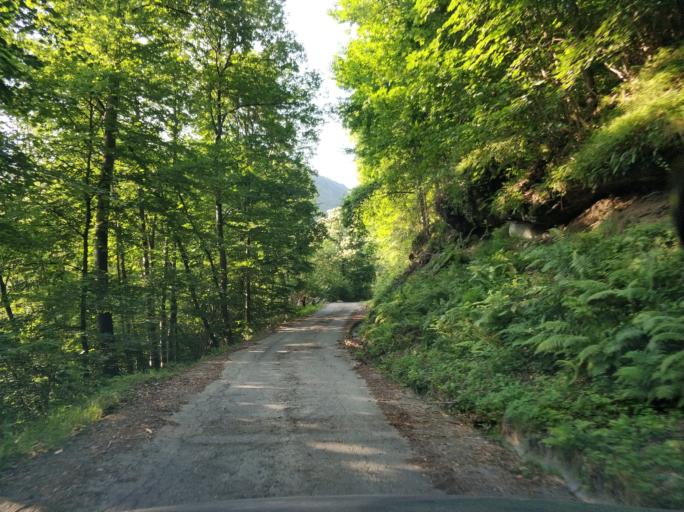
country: IT
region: Piedmont
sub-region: Provincia di Torino
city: Ceres
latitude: 45.3141
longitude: 7.3688
